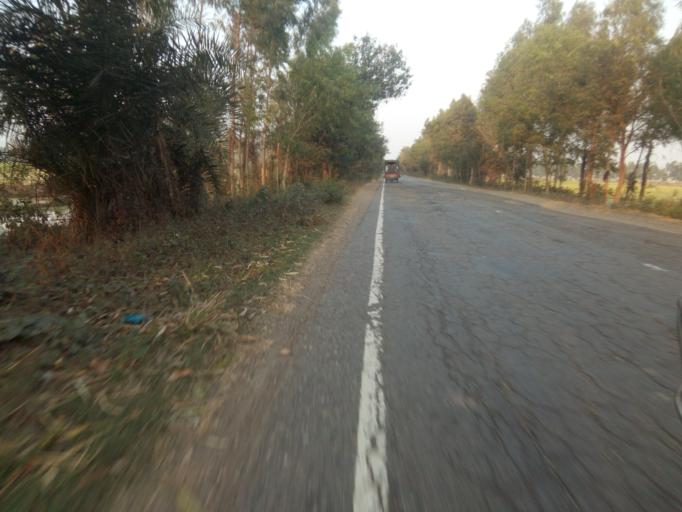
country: BD
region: Rajshahi
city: Bogra
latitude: 24.5677
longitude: 89.2110
